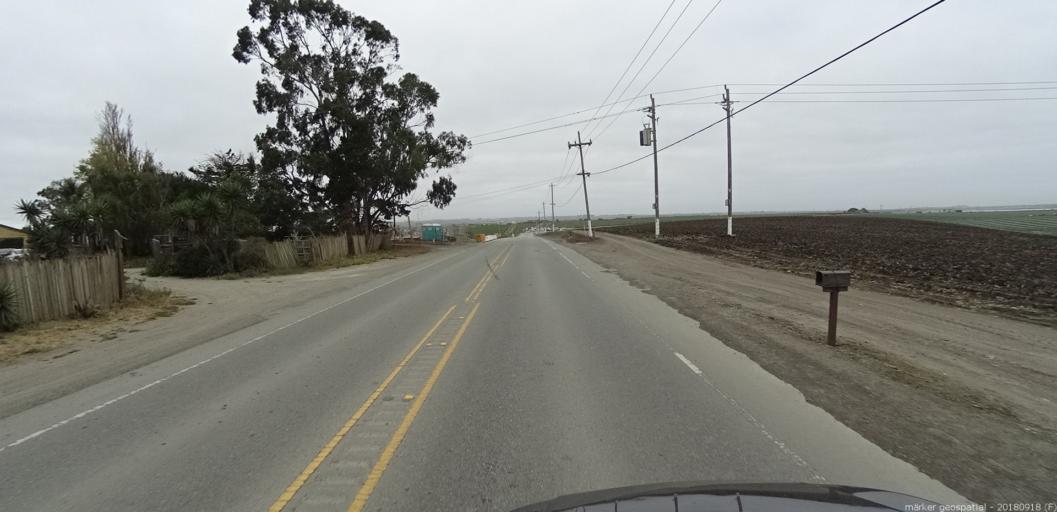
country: US
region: California
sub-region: Monterey County
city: Castroville
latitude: 36.7454
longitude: -121.7275
